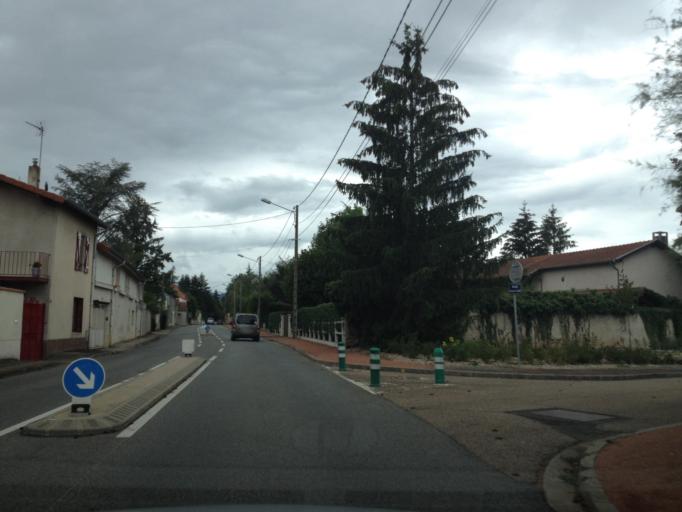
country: FR
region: Rhone-Alpes
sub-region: Departement de la Loire
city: Riorges
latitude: 46.0401
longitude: 4.0271
